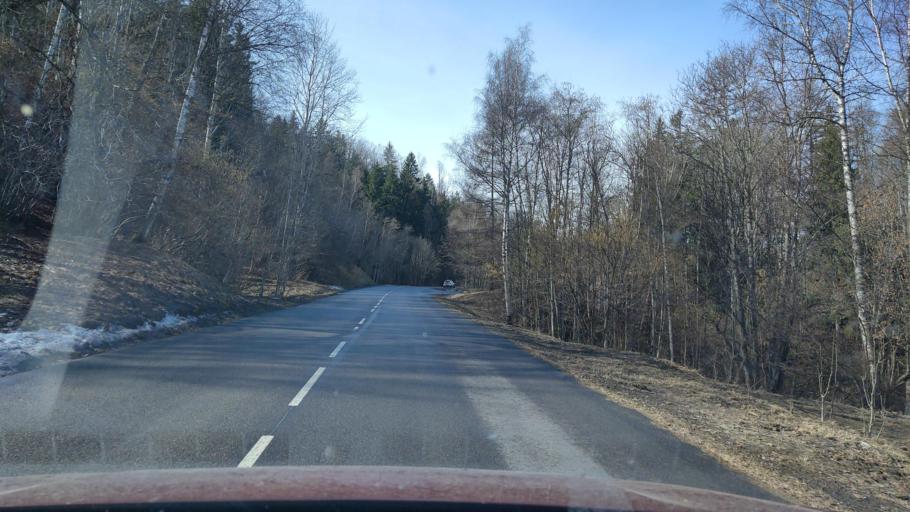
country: FR
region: Rhone-Alpes
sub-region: Departement de la Savoie
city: Macot-la-Plagne
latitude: 45.5655
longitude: 6.7225
